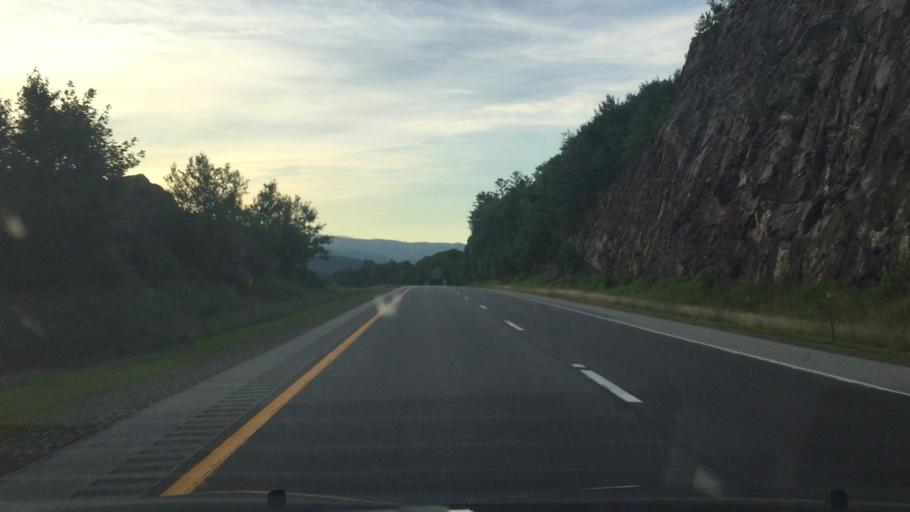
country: US
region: New Hampshire
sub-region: Grafton County
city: Thornton
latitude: 43.8566
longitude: -71.6500
